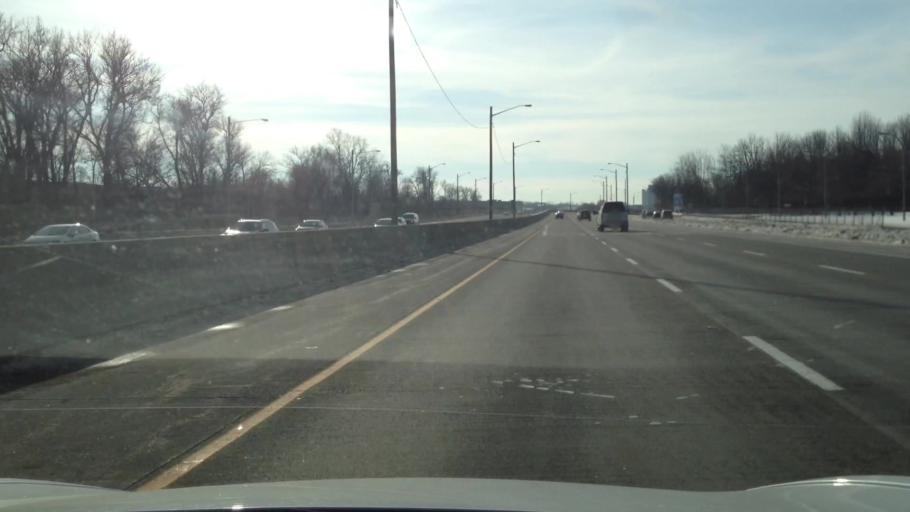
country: CA
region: Quebec
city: Baie-D'Urfe
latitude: 45.4231
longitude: -73.9248
